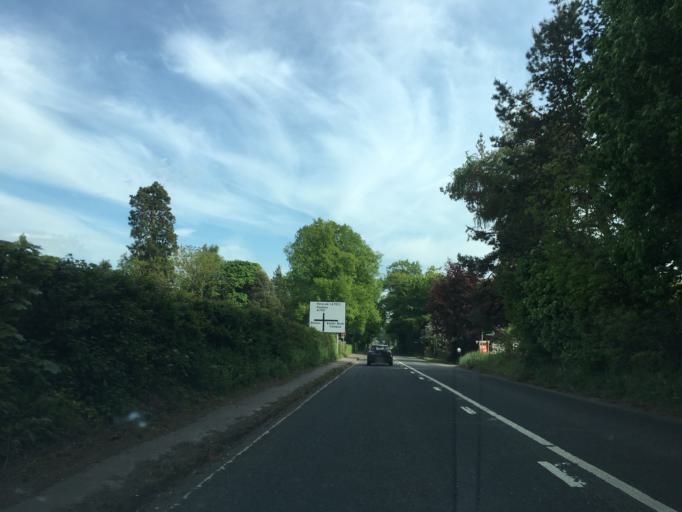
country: GB
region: Scotland
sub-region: Midlothian
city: Loanhead
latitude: 55.8719
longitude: -3.1927
